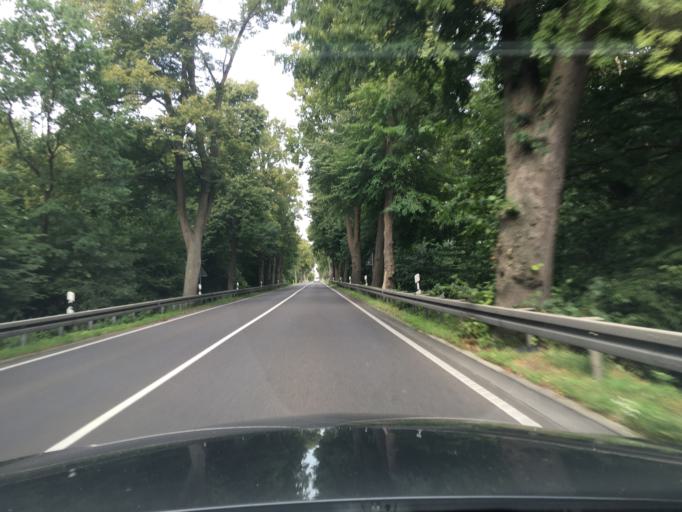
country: DE
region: Mecklenburg-Vorpommern
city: Wustrow
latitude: 53.4519
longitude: 13.1869
